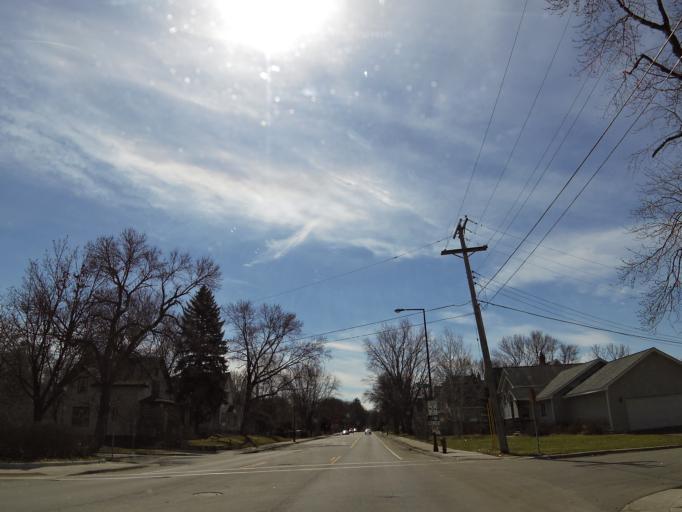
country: US
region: Minnesota
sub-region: Ramsey County
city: Maplewood
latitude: 44.9692
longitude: -93.0451
